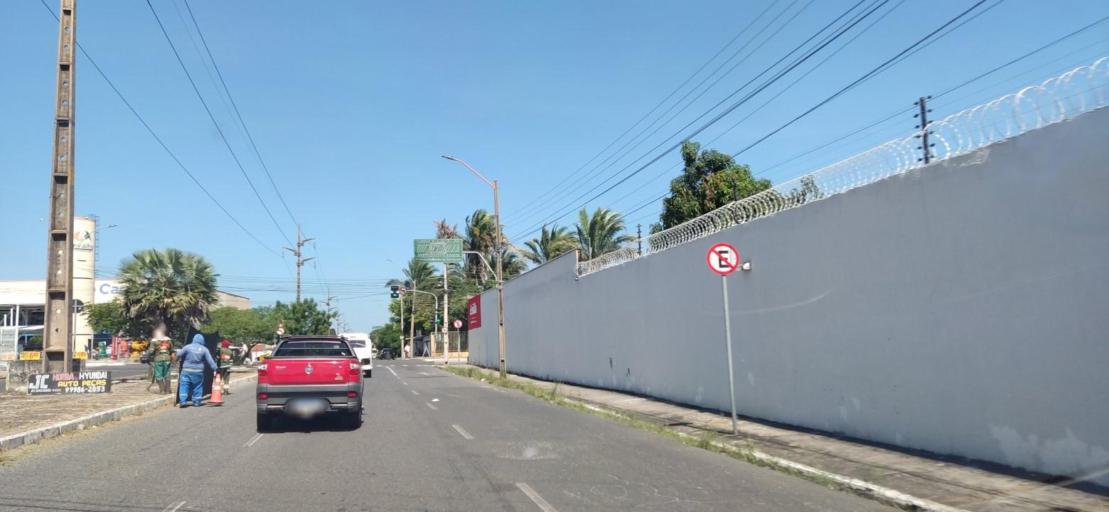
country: BR
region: Piaui
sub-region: Teresina
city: Teresina
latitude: -5.1191
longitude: -42.8024
